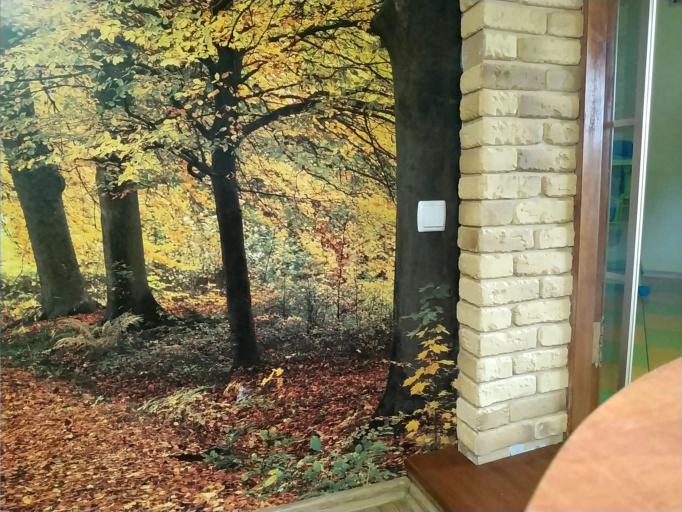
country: RU
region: Smolensk
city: Dorogobuzh
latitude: 54.9440
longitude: 33.2994
